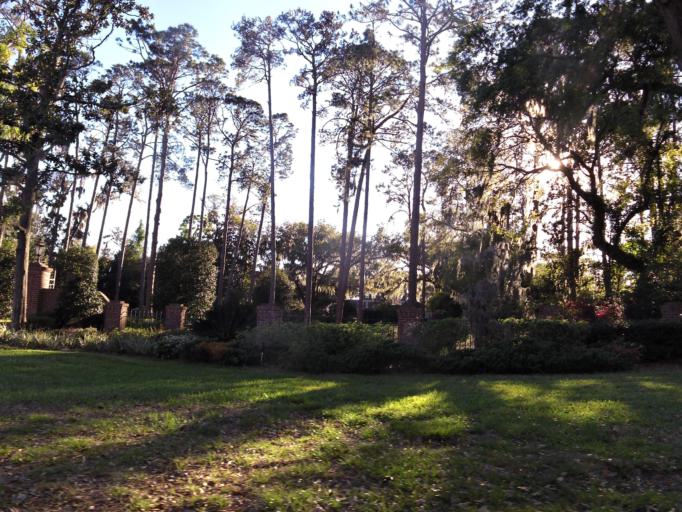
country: US
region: Florida
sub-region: Duval County
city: Jacksonville
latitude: 30.2575
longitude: -81.6449
